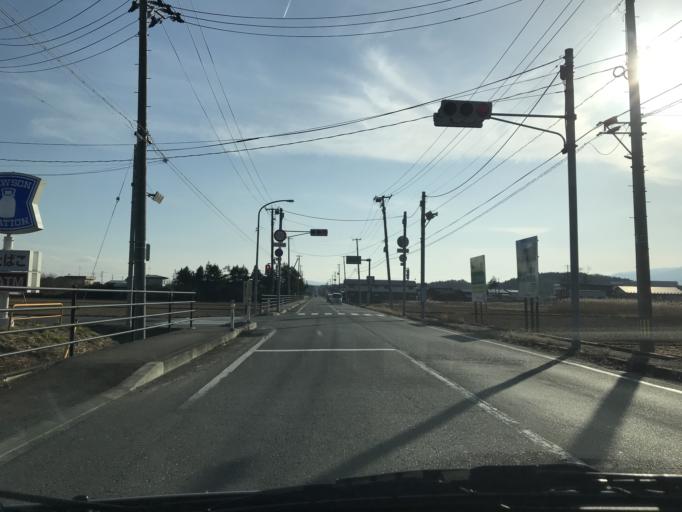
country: JP
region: Iwate
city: Kitakami
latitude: 39.2549
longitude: 141.1102
